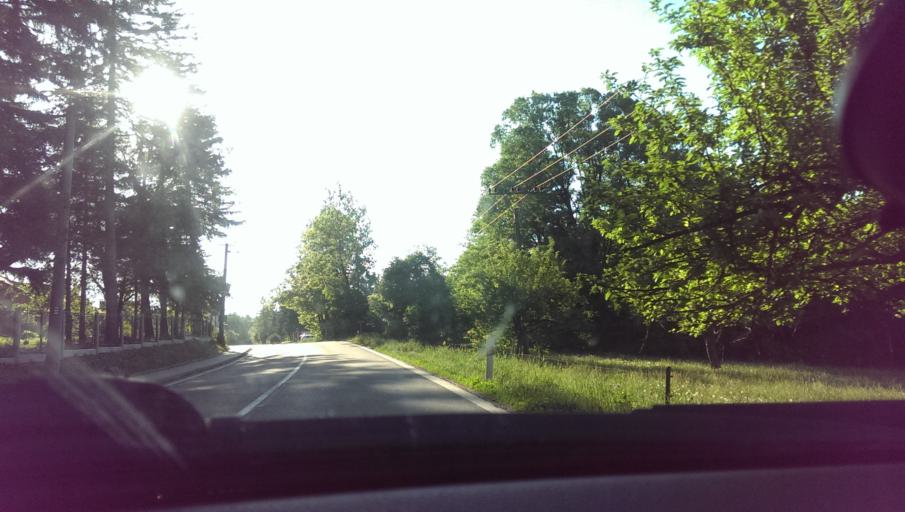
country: CZ
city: Kuncice pod Ondrejnikem
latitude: 49.5390
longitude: 18.2929
